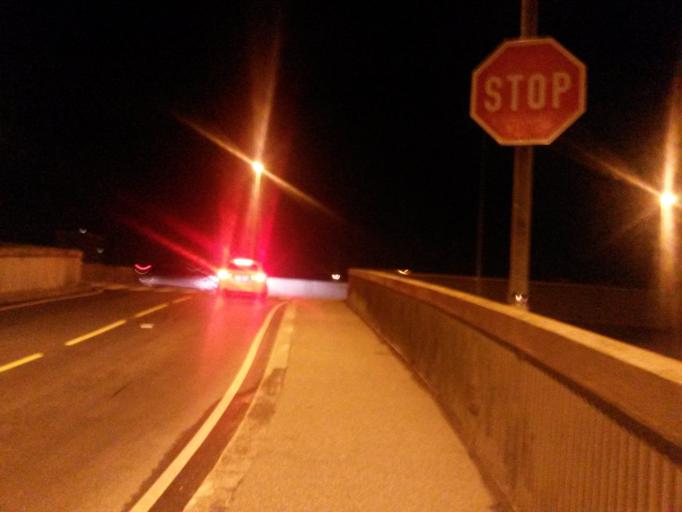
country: NO
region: Rogaland
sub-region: Stavanger
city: Stavanger
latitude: 58.9553
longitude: 5.7458
